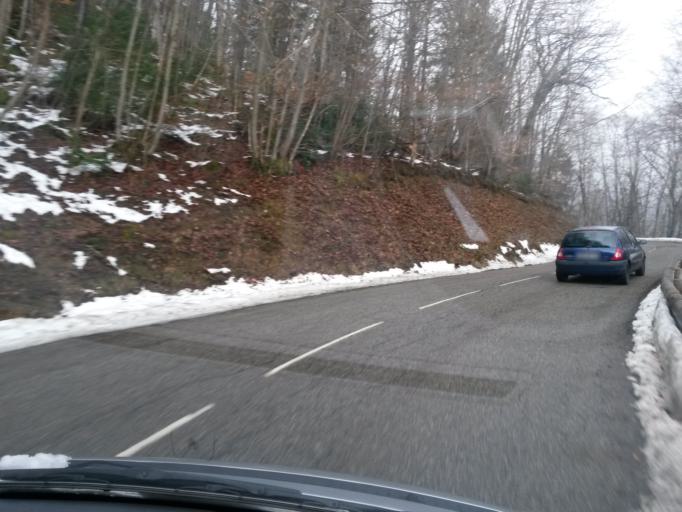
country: FR
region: Rhone-Alpes
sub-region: Departement de l'Isere
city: La Terrasse
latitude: 45.3303
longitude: 5.9165
